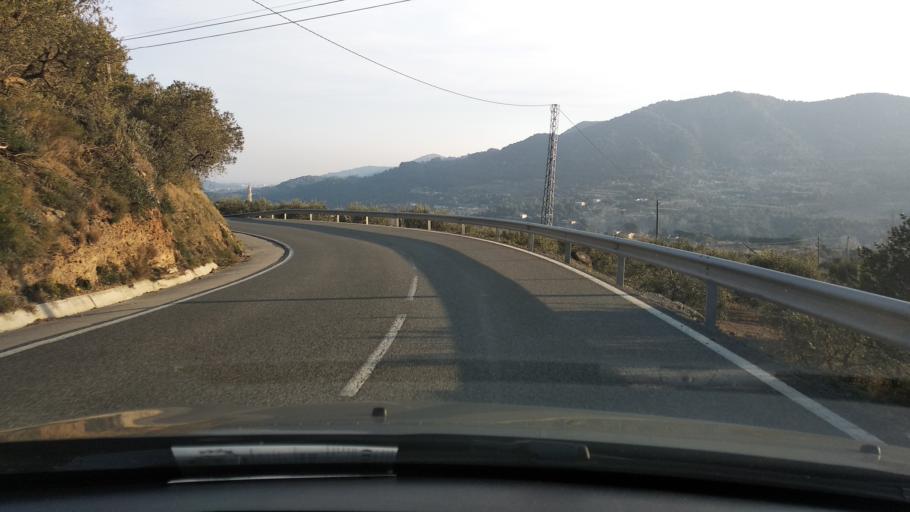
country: ES
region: Catalonia
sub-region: Provincia de Tarragona
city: Alforja
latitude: 41.2174
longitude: 0.9658
